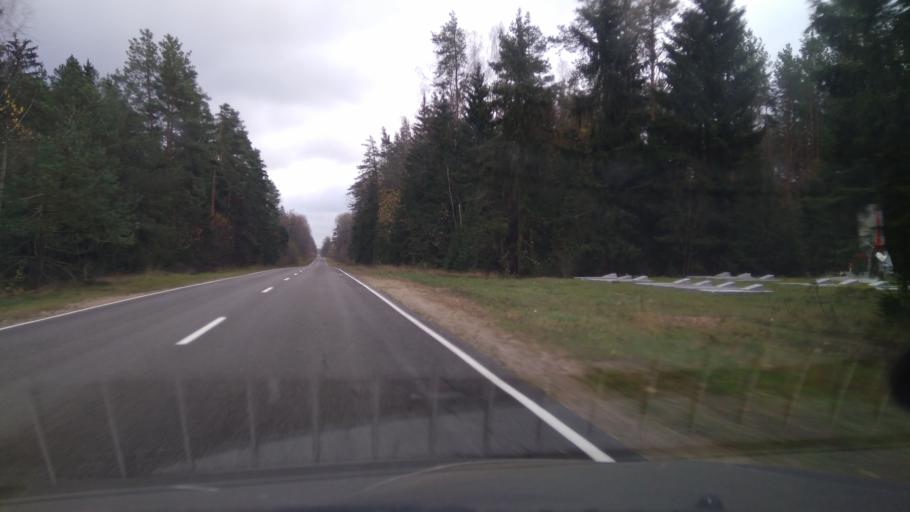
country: BY
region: Minsk
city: Urechcha
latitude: 53.2125
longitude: 27.8784
